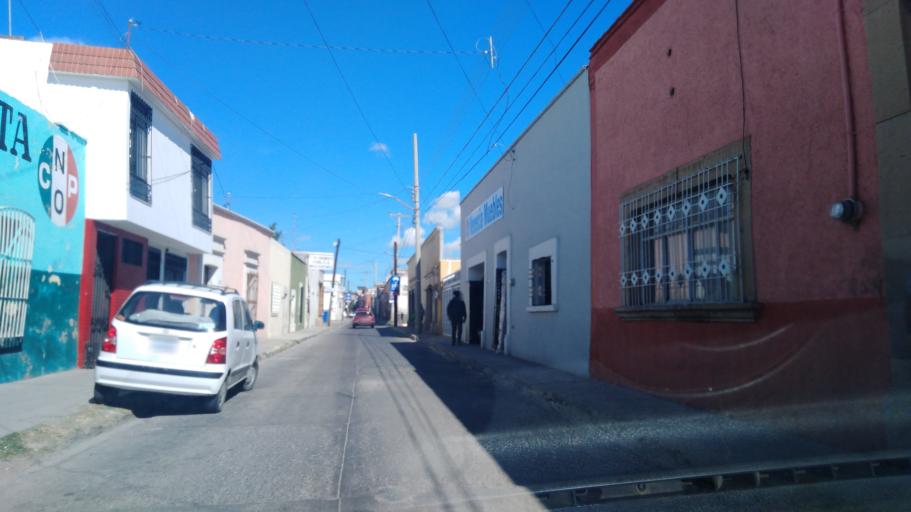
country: MX
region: Durango
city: Victoria de Durango
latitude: 24.0215
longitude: -104.6640
